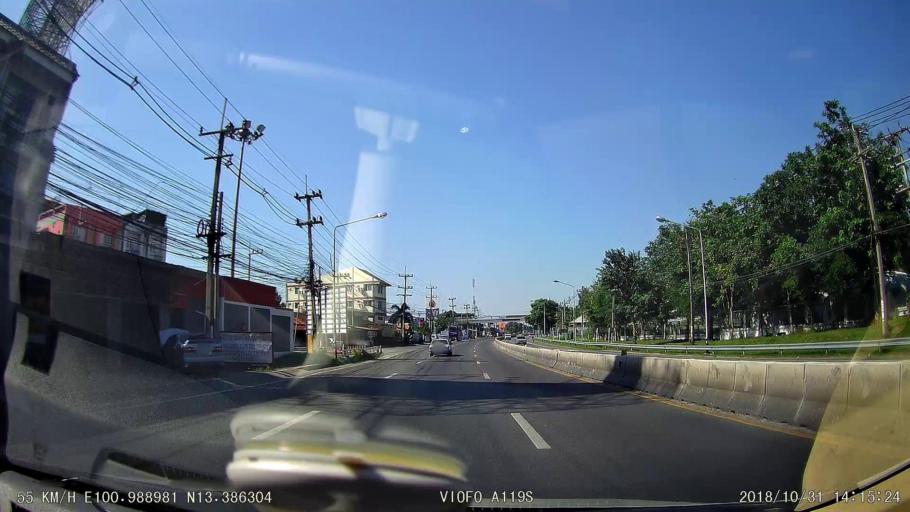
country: TH
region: Chon Buri
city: Chon Buri
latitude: 13.3866
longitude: 100.9887
